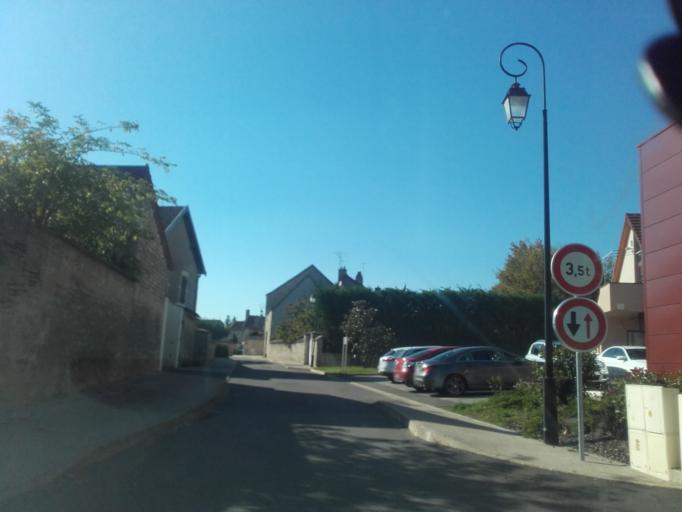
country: FR
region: Bourgogne
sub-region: Departement de la Cote-d'Or
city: Corpeau
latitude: 46.9452
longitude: 4.7561
